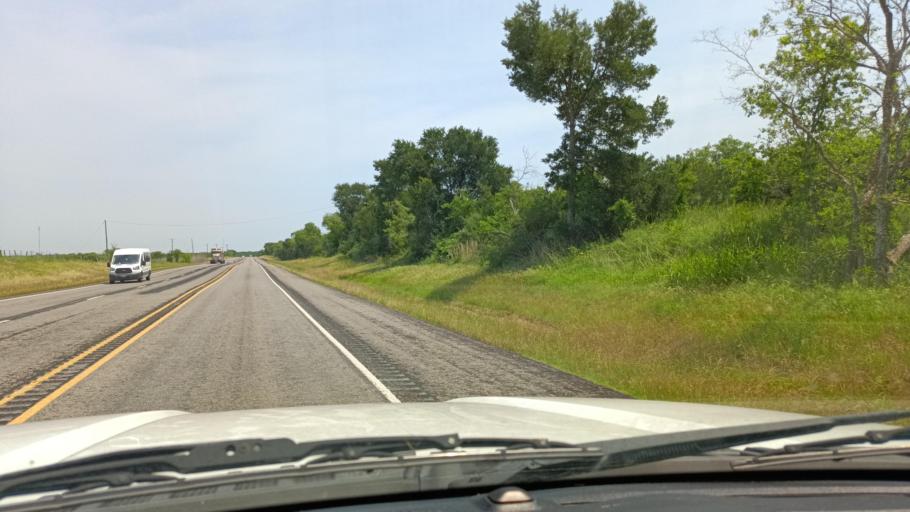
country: US
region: Texas
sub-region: Bell County
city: Rogers
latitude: 30.8876
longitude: -97.1556
